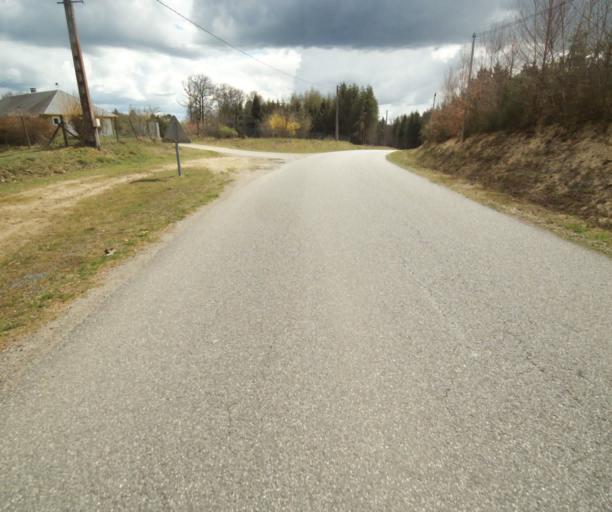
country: FR
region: Limousin
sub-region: Departement de la Correze
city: Correze
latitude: 45.2730
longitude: 1.9697
